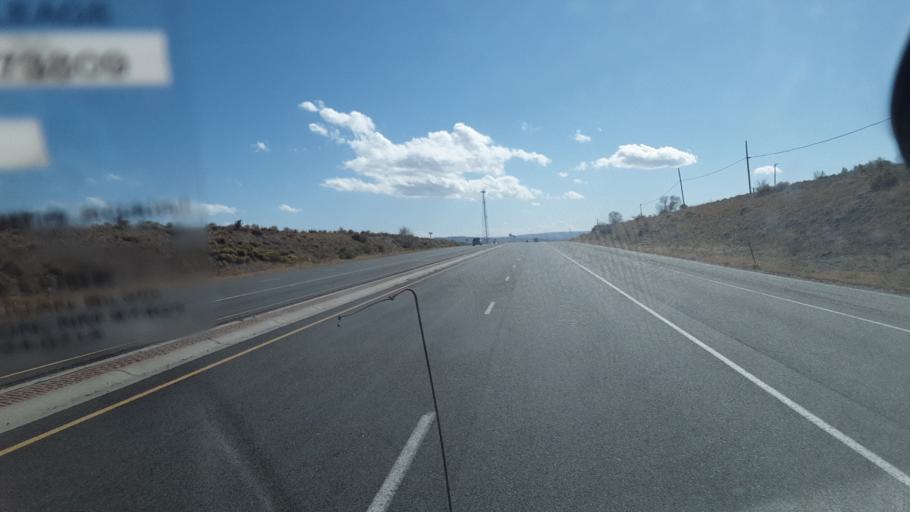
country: US
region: New Mexico
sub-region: Rio Arriba County
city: Espanola
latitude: 36.0209
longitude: -106.0911
